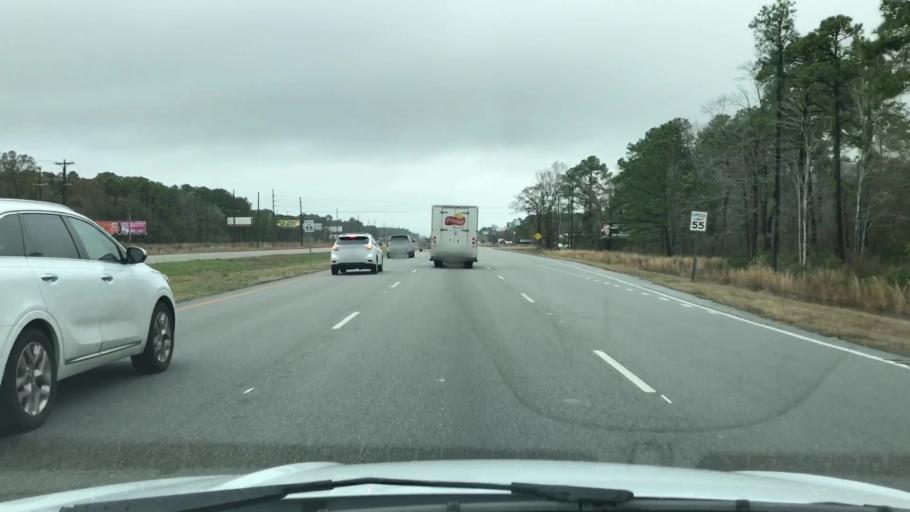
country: US
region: South Carolina
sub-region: Horry County
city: Forestbrook
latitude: 33.7701
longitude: -78.9782
